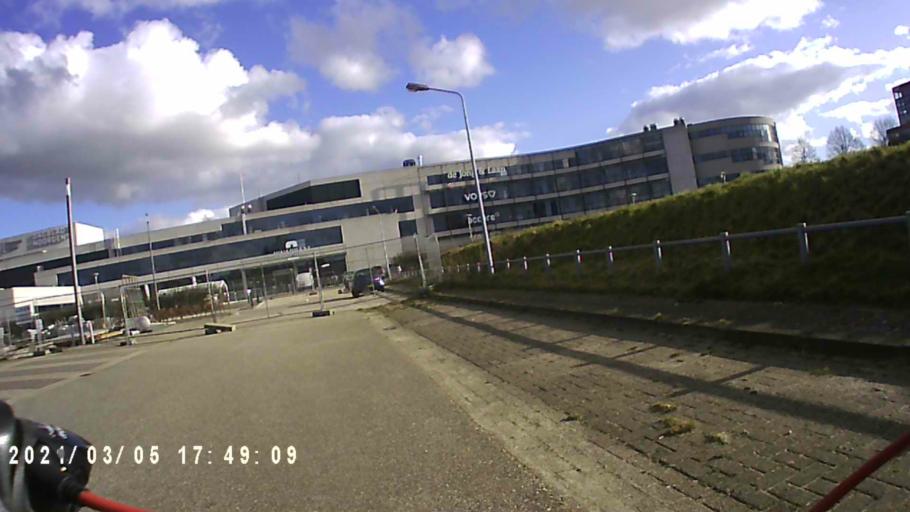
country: NL
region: Groningen
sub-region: Gemeente Groningen
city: Oosterpark
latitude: 53.2136
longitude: 6.5871
